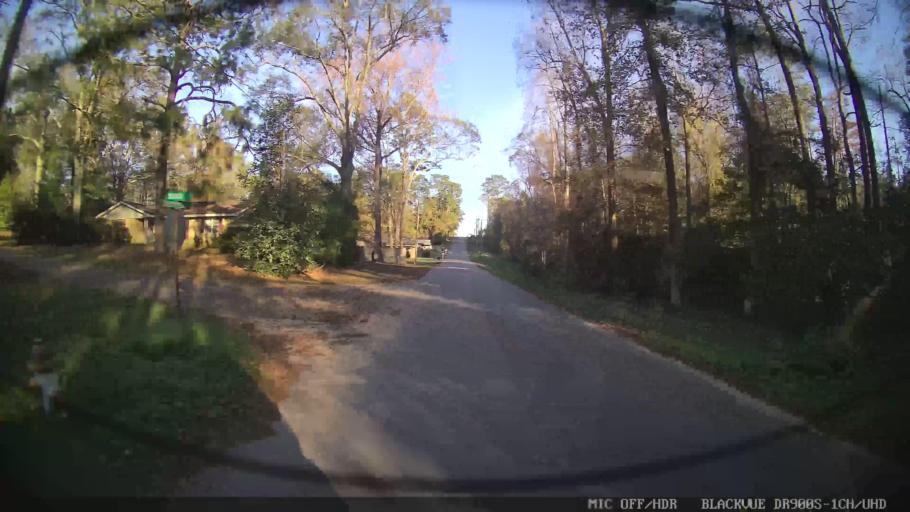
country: US
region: Mississippi
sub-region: Lamar County
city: Purvis
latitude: 31.1435
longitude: -89.4184
